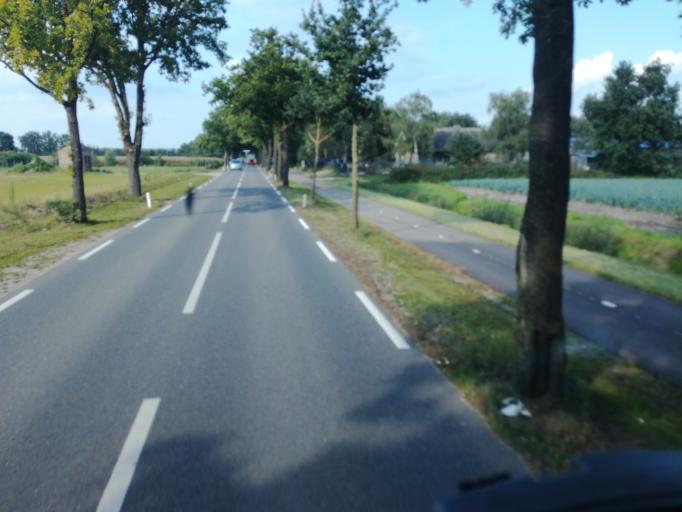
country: NL
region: North Brabant
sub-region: Gemeente Uden
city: Volkel
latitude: 51.6522
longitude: 5.6732
